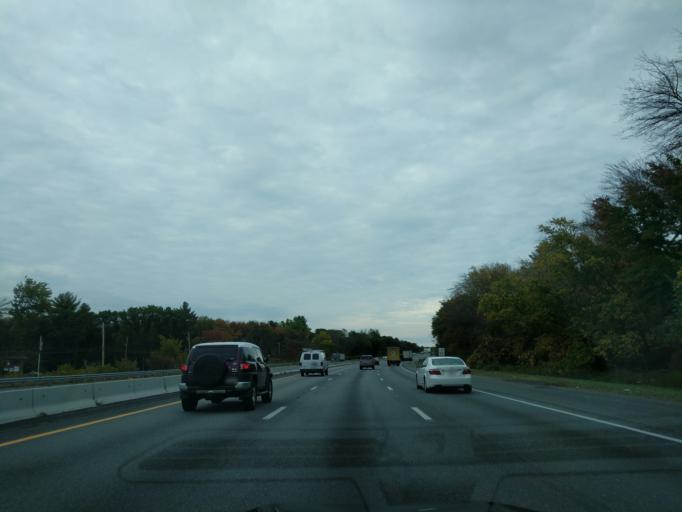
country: US
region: Massachusetts
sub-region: Middlesex County
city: Wakefield
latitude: 42.5268
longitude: -71.0725
